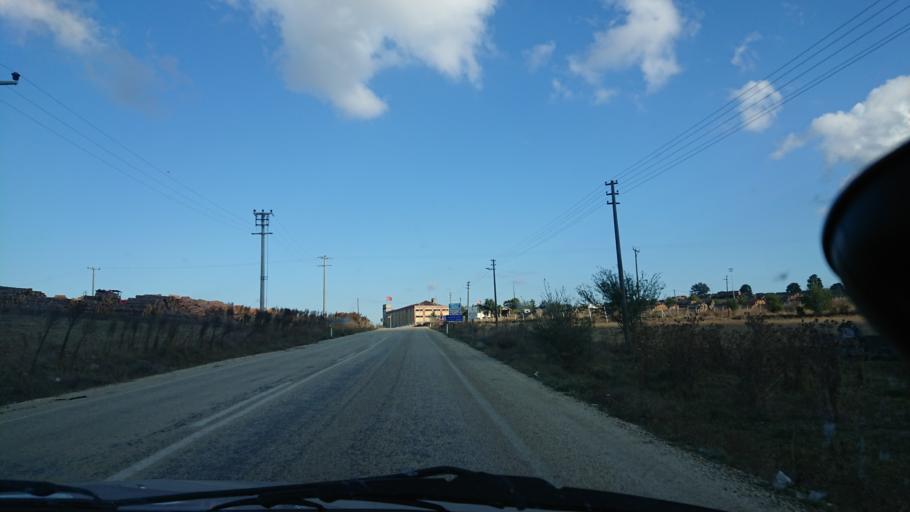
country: TR
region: Bilecik
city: Pazaryeri
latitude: 40.0007
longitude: 29.8859
